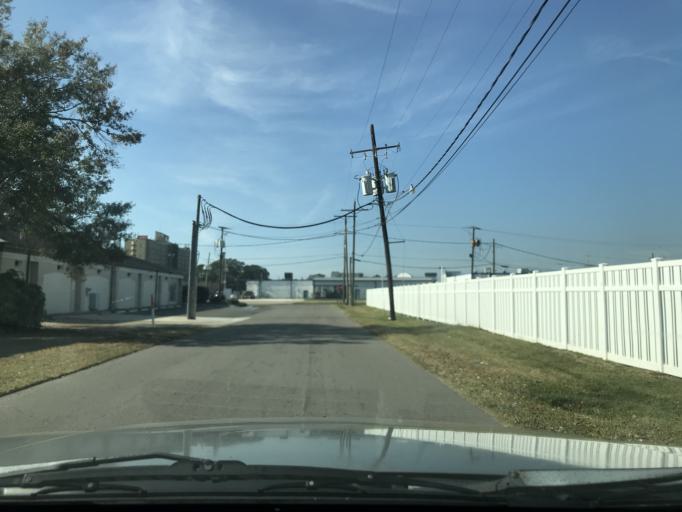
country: US
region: Louisiana
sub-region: Jefferson Parish
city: Marrero
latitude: 29.8940
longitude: -90.0938
